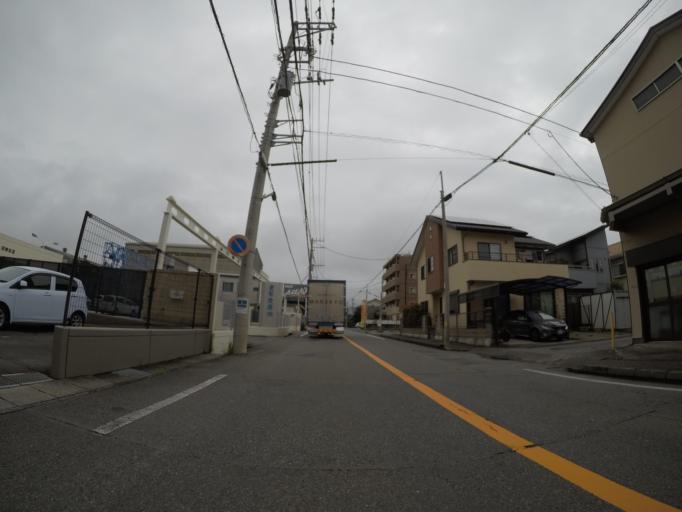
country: JP
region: Shizuoka
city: Numazu
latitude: 35.1144
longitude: 138.8525
